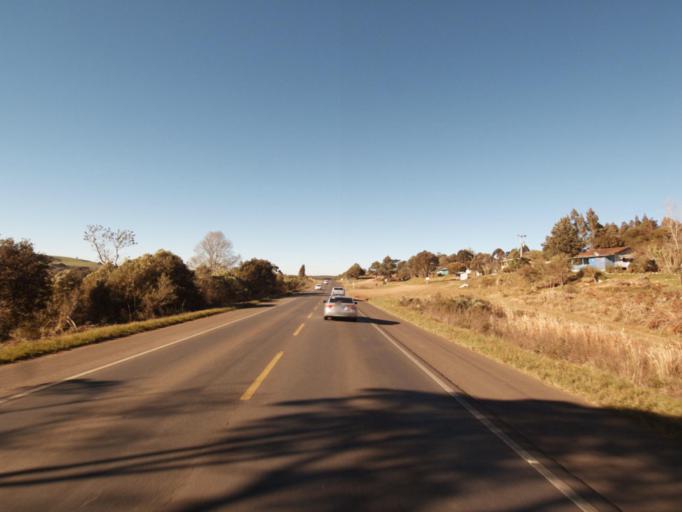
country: BR
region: Santa Catarina
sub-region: Concordia
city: Concordia
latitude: -26.9039
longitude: -51.9714
